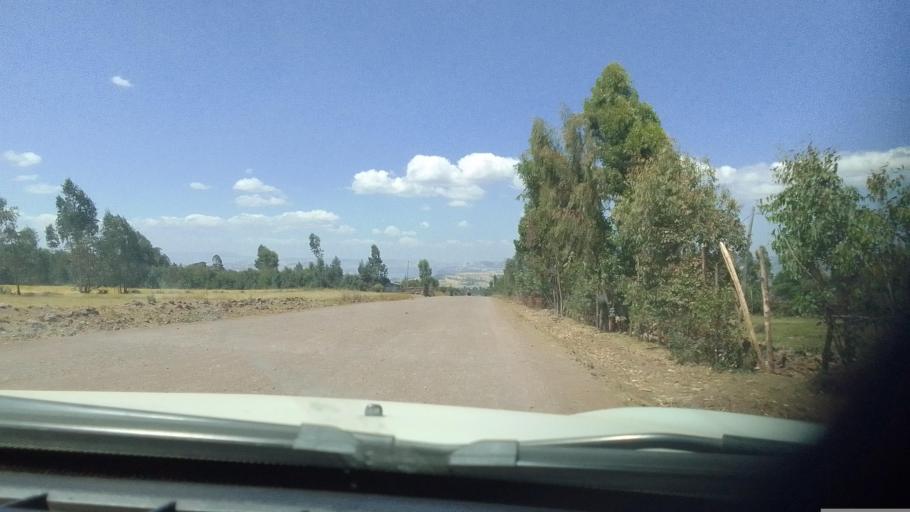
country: ET
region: Oromiya
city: Hagere Hiywet
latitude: 8.9223
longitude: 37.8648
